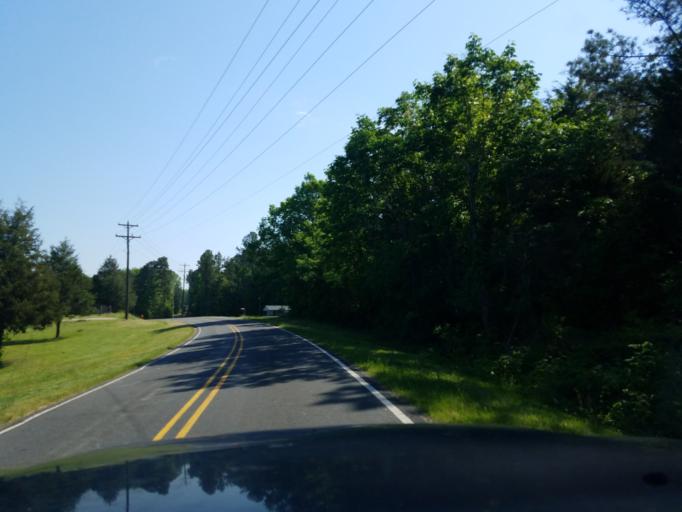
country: US
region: North Carolina
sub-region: Vance County
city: Henderson
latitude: 36.3908
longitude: -78.4423
